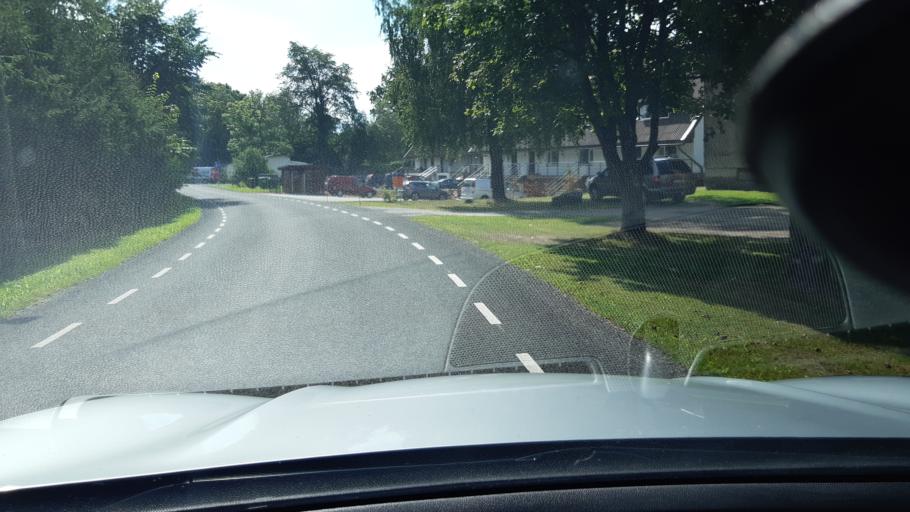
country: EE
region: Raplamaa
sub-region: Kehtna vald
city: Kehtna
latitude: 58.9410
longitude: 24.8982
